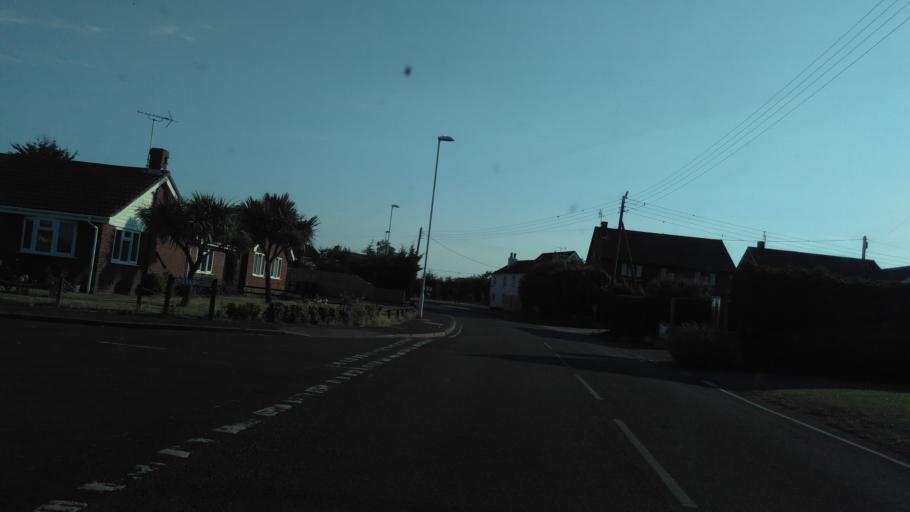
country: GB
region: England
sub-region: Kent
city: Whitstable
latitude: 51.3466
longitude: 1.0026
